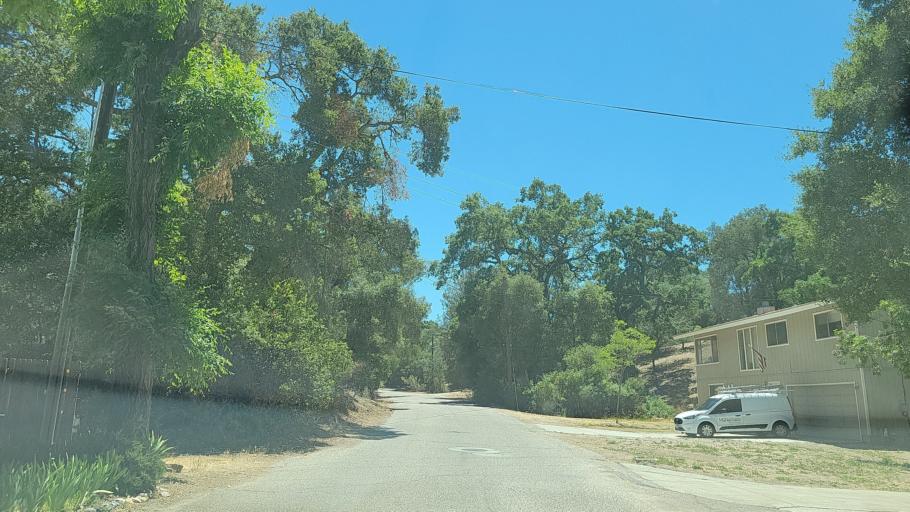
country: US
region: California
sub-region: San Luis Obispo County
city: Atascadero
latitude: 35.4769
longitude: -120.6626
